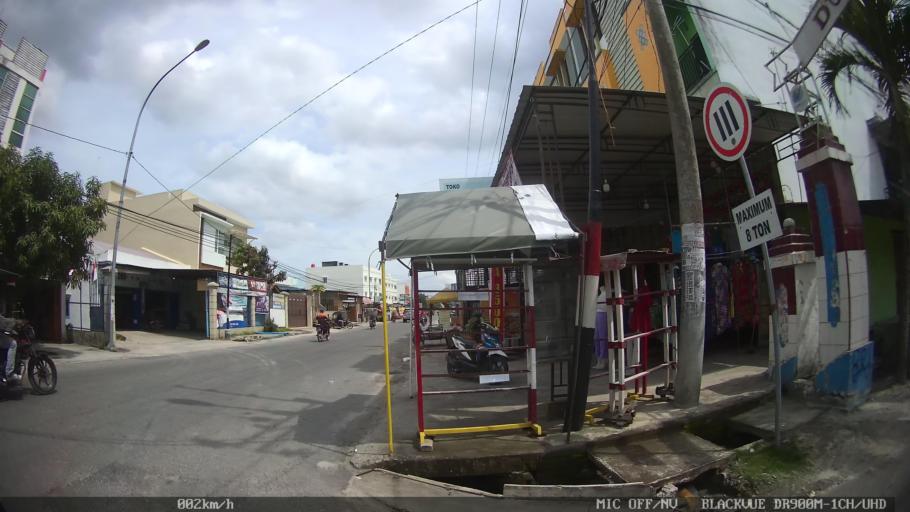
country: ID
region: North Sumatra
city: Percut
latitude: 3.5728
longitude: 98.8688
